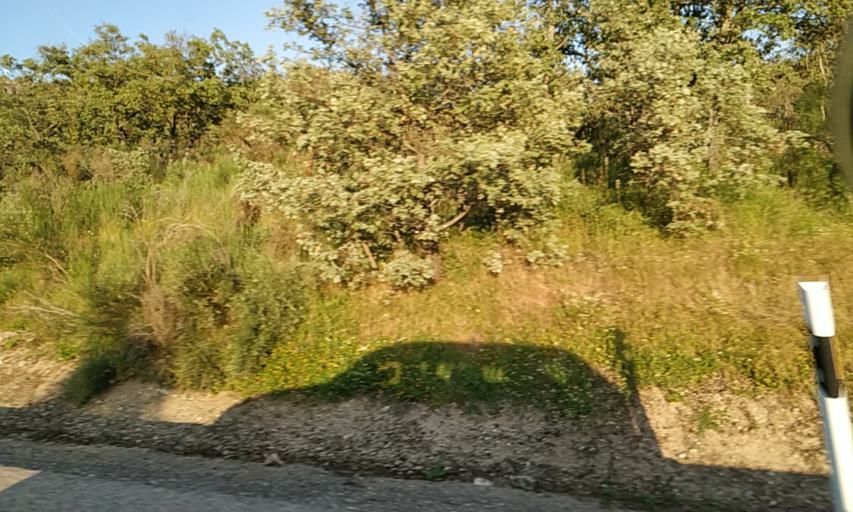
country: ES
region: Extremadura
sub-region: Provincia de Caceres
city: Valencia de Alcantara
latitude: 39.3788
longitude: -7.2519
